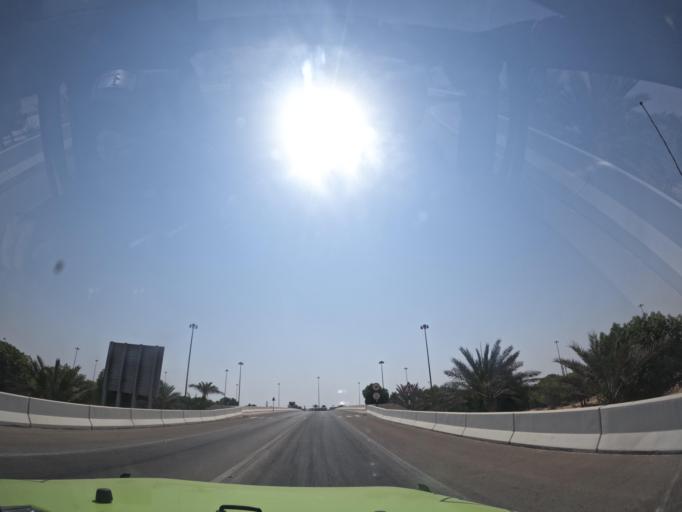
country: AE
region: Abu Dhabi
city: Al Ain
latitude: 24.1766
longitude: 55.1342
